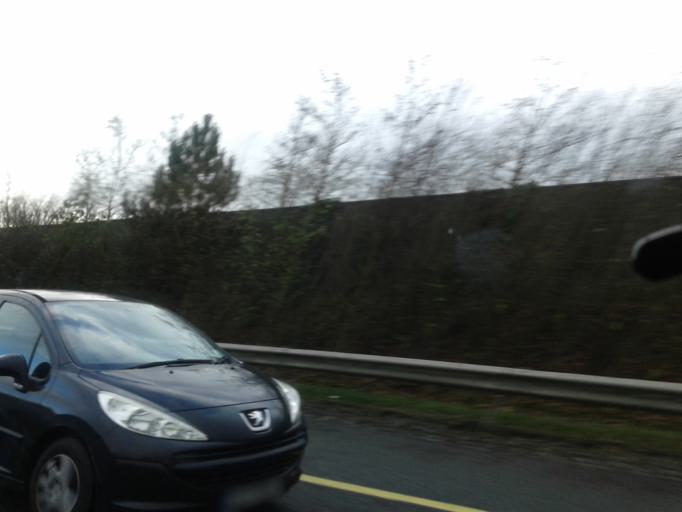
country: IE
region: Leinster
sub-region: An Mhi
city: Ashbourne
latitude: 53.4790
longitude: -6.3720
